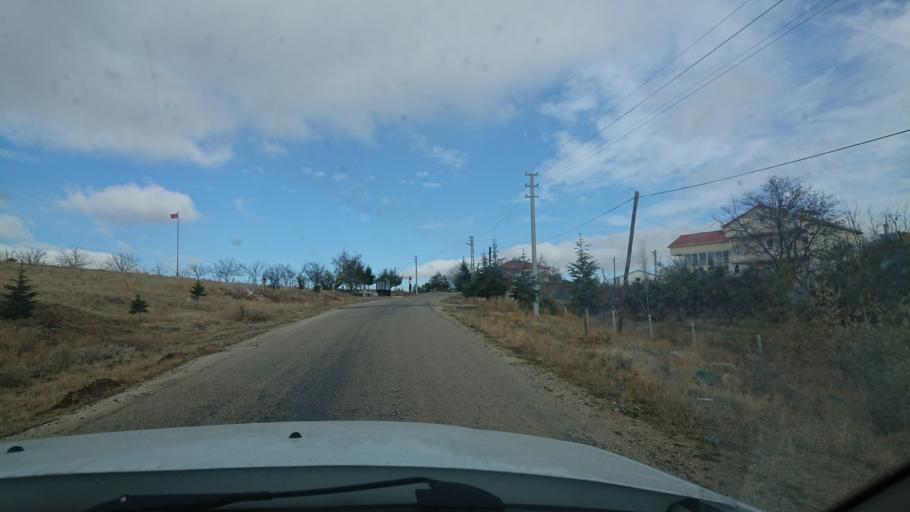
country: TR
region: Aksaray
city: Agacoren
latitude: 38.8257
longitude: 33.9578
